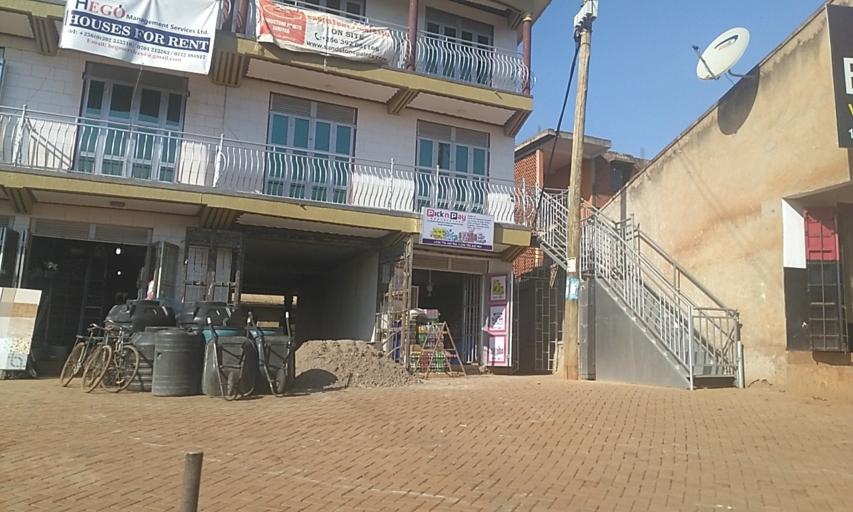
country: UG
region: Central Region
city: Kampala Central Division
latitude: 0.3306
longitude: 32.5301
